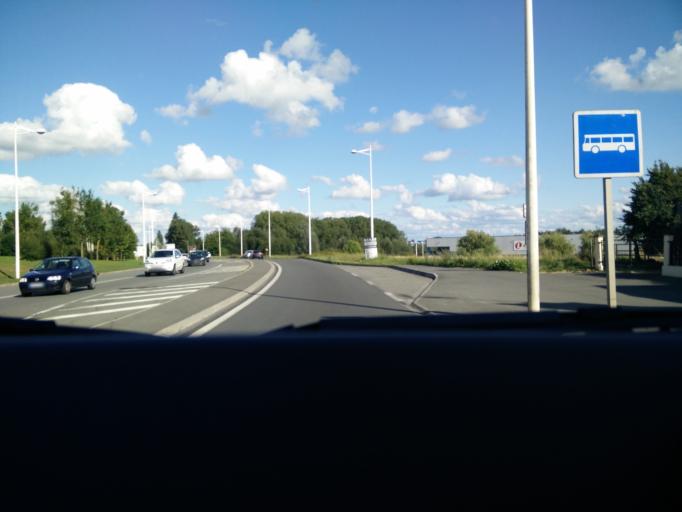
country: FR
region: Nord-Pas-de-Calais
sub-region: Departement du Nord
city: Feignies
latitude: 50.2798
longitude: 3.9101
